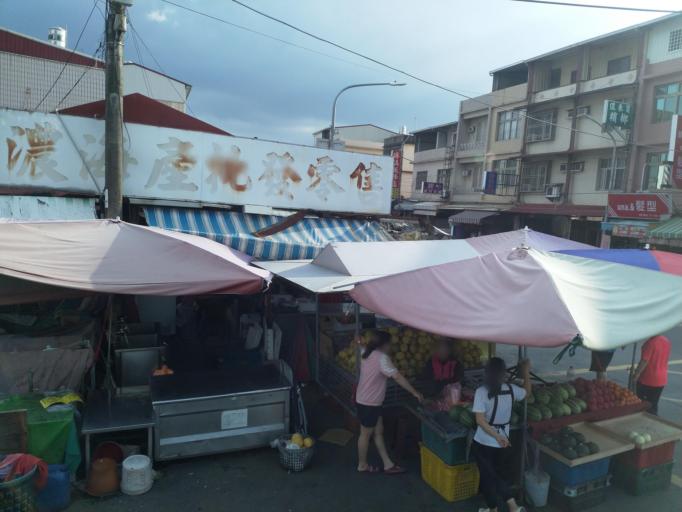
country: TW
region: Taiwan
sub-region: Pingtung
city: Pingtung
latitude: 22.8985
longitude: 120.5423
